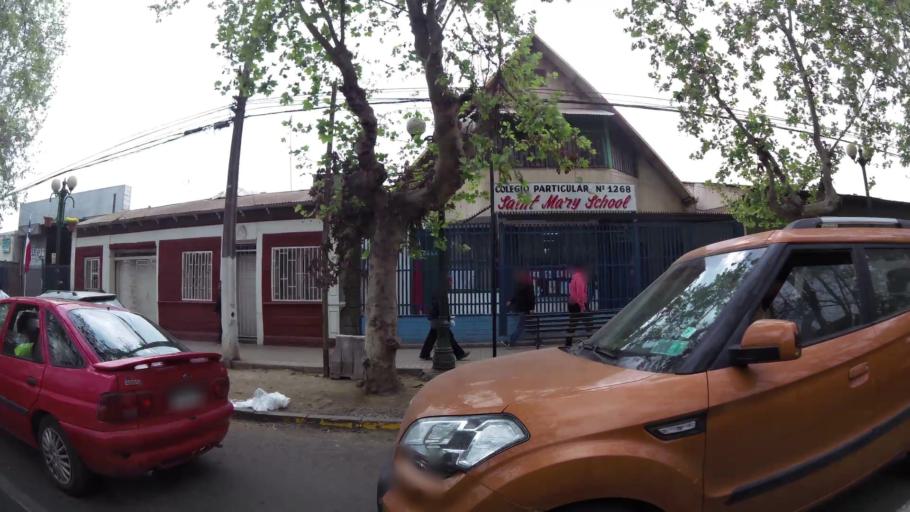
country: CL
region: Santiago Metropolitan
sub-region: Provincia de Chacabuco
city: Chicureo Abajo
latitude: -33.2046
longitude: -70.6747
